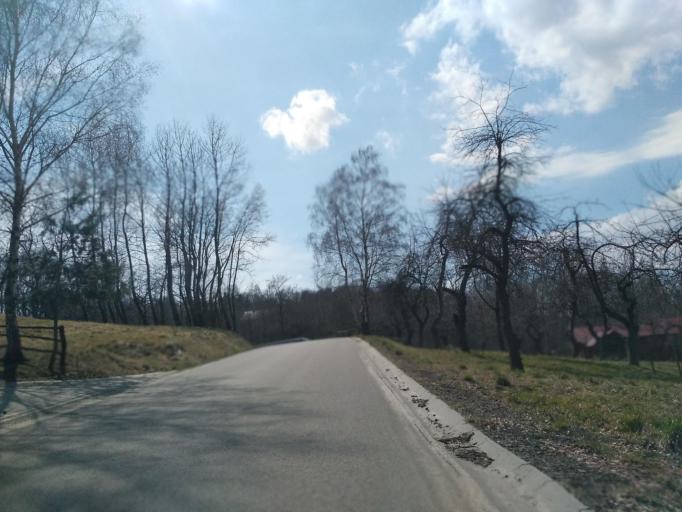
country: PL
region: Subcarpathian Voivodeship
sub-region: Powiat ropczycko-sedziszowski
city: Iwierzyce
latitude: 49.9909
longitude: 21.7369
